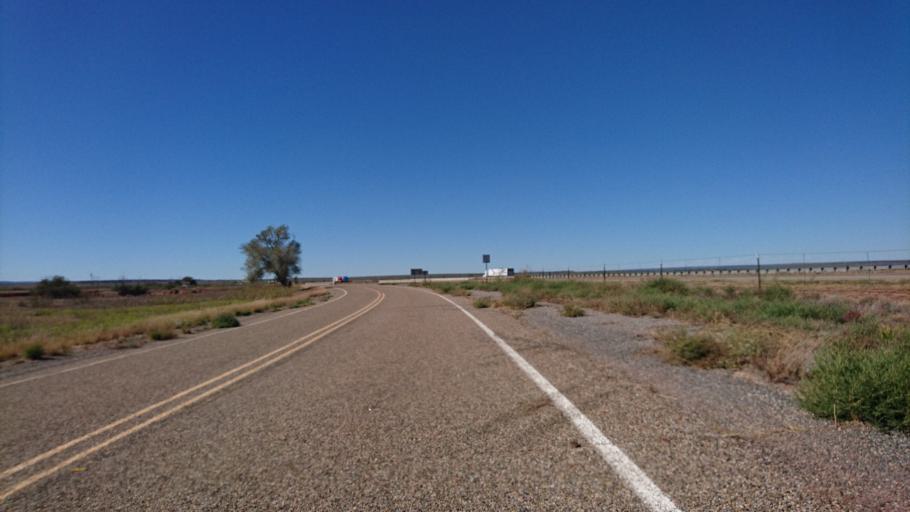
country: US
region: New Mexico
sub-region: Quay County
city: Tucumcari
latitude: 35.0917
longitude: -104.0745
